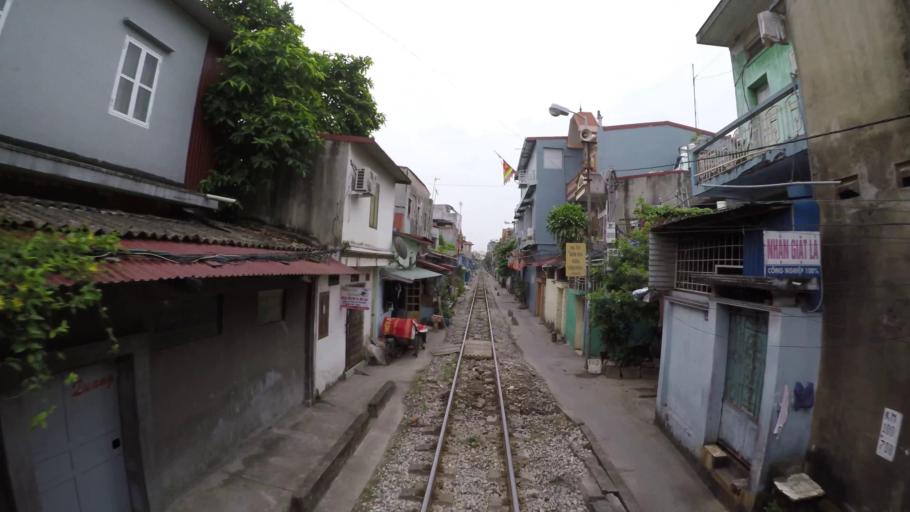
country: VN
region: Hai Phong
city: Haiphong
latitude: 20.8580
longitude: 106.6644
